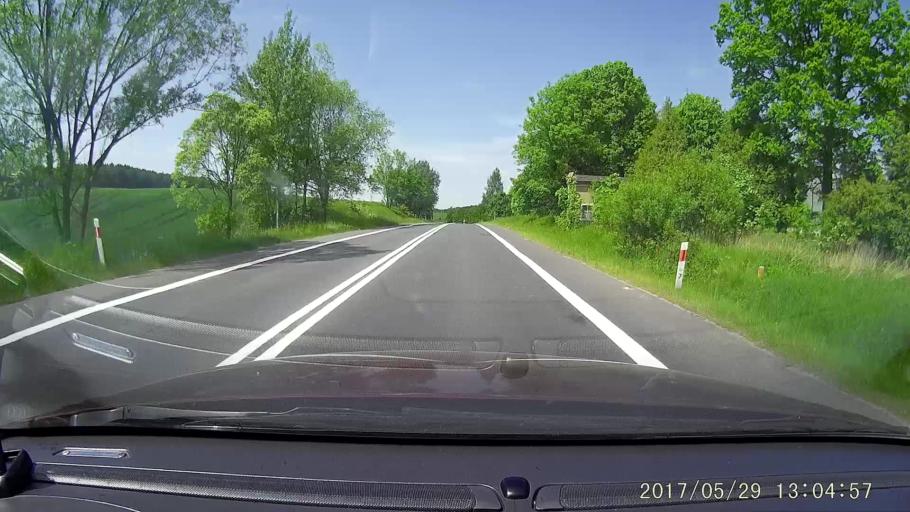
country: PL
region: Lower Silesian Voivodeship
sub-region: Powiat jeleniogorski
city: Stara Kamienica
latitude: 50.9387
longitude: 15.5952
